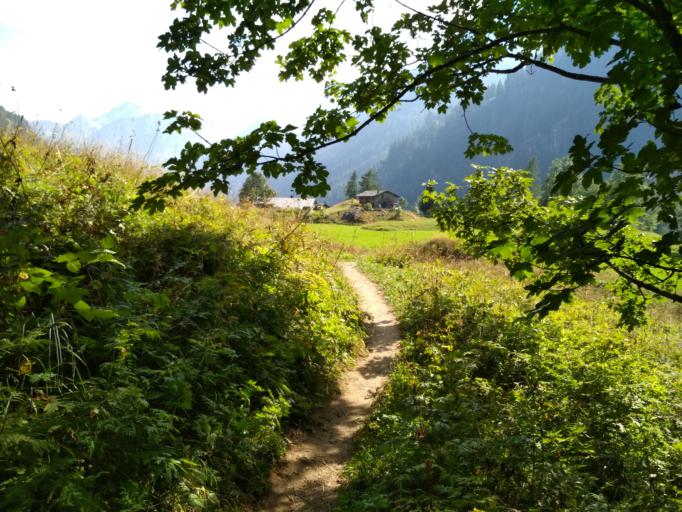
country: IT
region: Aosta Valley
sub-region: Valle d'Aosta
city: Gressoney-La-Trinite
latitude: 45.8106
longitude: 7.8266
